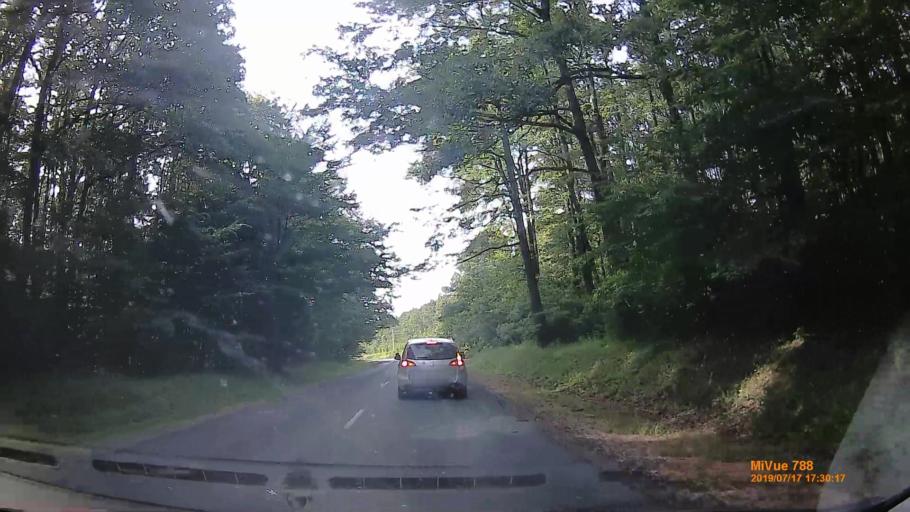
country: HU
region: Veszprem
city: Ajka
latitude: 47.0228
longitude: 17.5745
